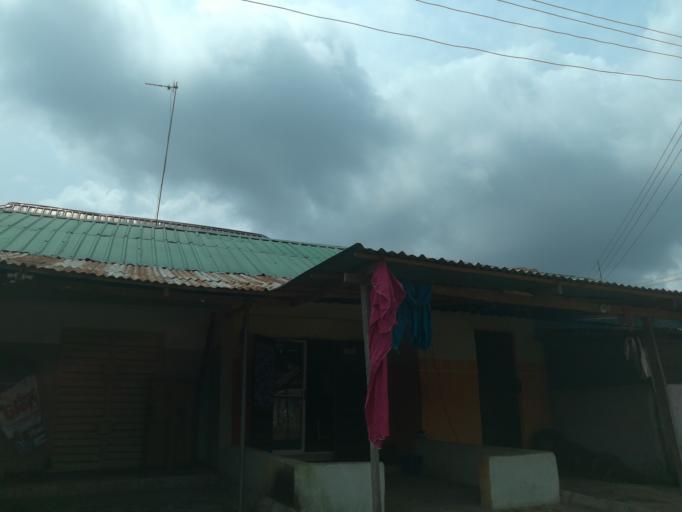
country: NG
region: Rivers
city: Port Harcourt
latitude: 4.8924
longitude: 6.9833
